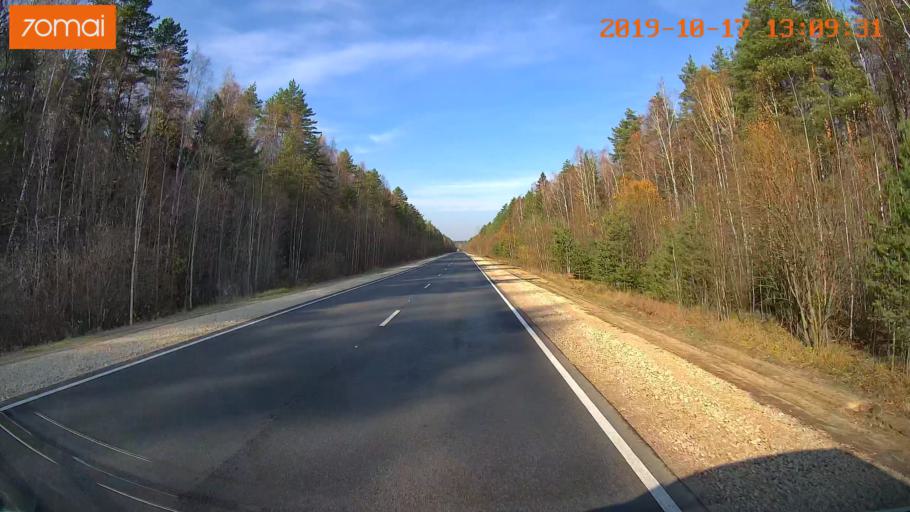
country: RU
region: Rjazan
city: Syntul
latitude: 55.0050
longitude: 41.2626
